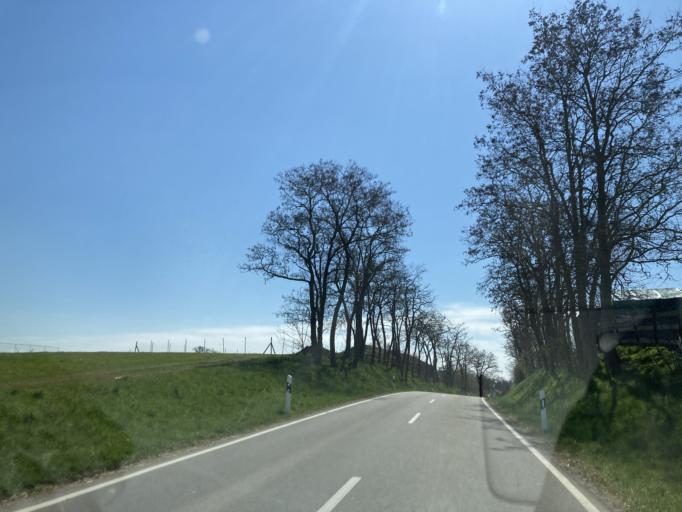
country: DE
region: Baden-Wuerttemberg
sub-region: Regierungsbezirk Stuttgart
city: Bondorf
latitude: 48.4941
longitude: 8.8462
